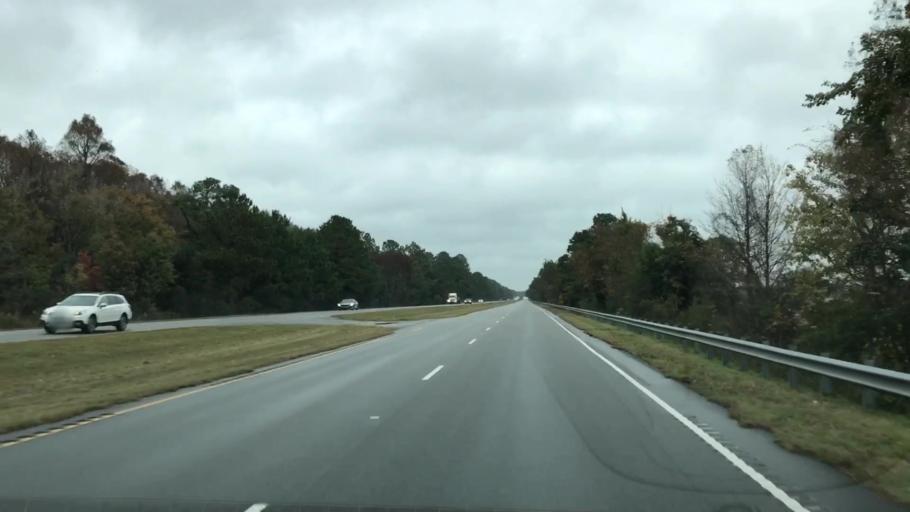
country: US
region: South Carolina
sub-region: Georgetown County
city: Georgetown
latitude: 33.1936
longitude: -79.3974
